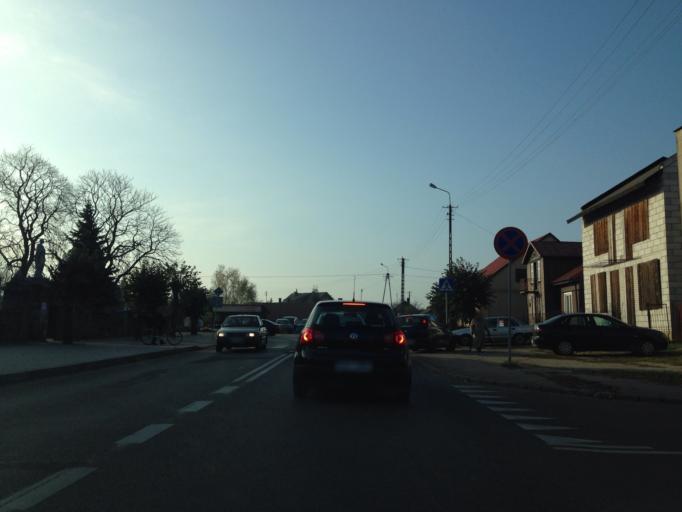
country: PL
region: Masovian Voivodeship
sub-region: Powiat zurominski
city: Biezun
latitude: 52.9589
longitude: 19.8923
